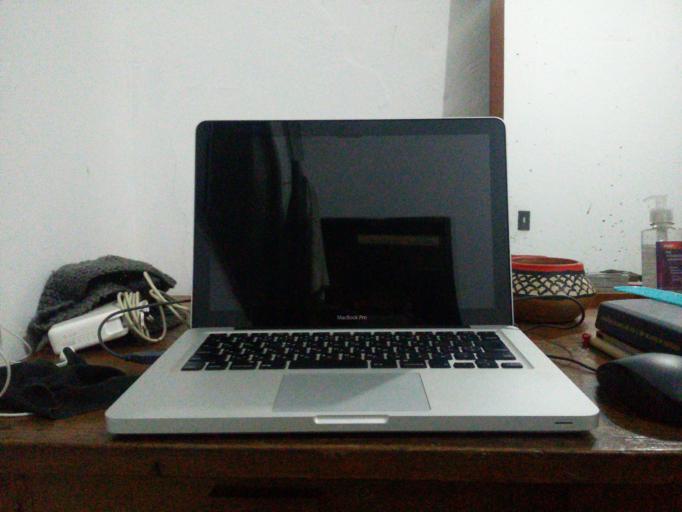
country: BR
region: Sao Paulo
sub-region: Presidente Prudente
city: Presidente Prudente
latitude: -22.1186
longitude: -51.4112
